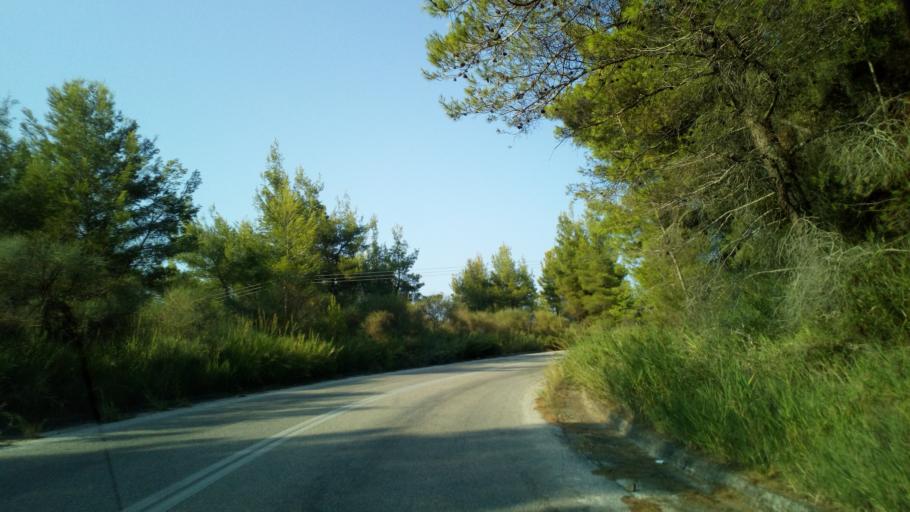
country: GR
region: Central Macedonia
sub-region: Nomos Chalkidikis
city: Neos Marmaras
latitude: 40.1756
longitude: 23.8377
